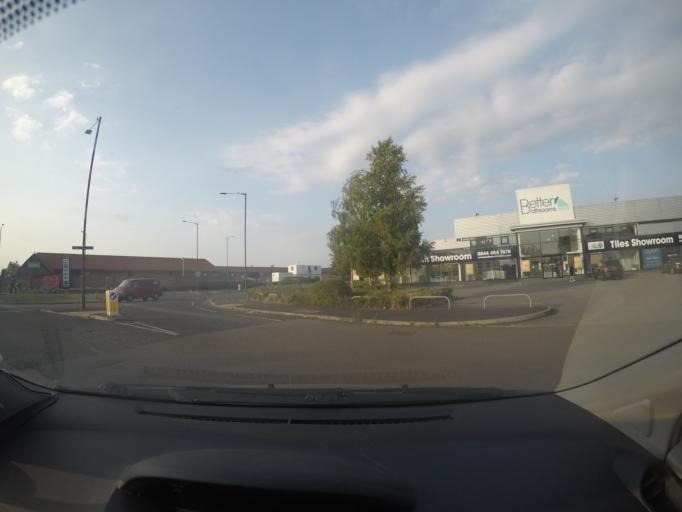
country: GB
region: England
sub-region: City of York
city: Wigginton
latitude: 53.9915
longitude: -1.0993
